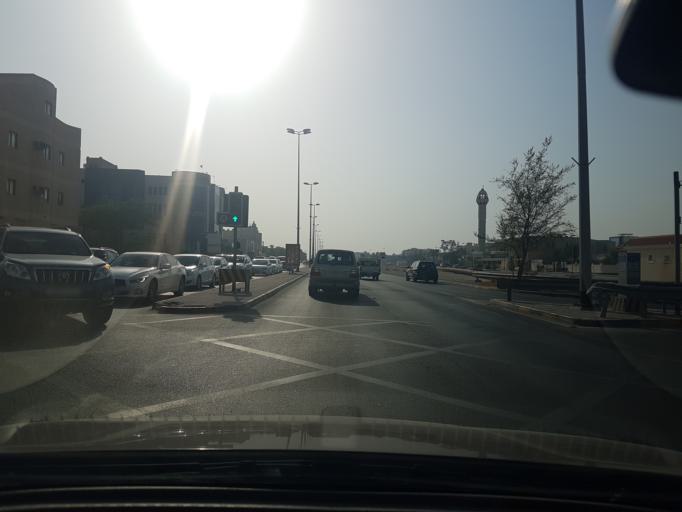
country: BH
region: Northern
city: Ar Rifa'
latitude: 26.1272
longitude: 50.5589
